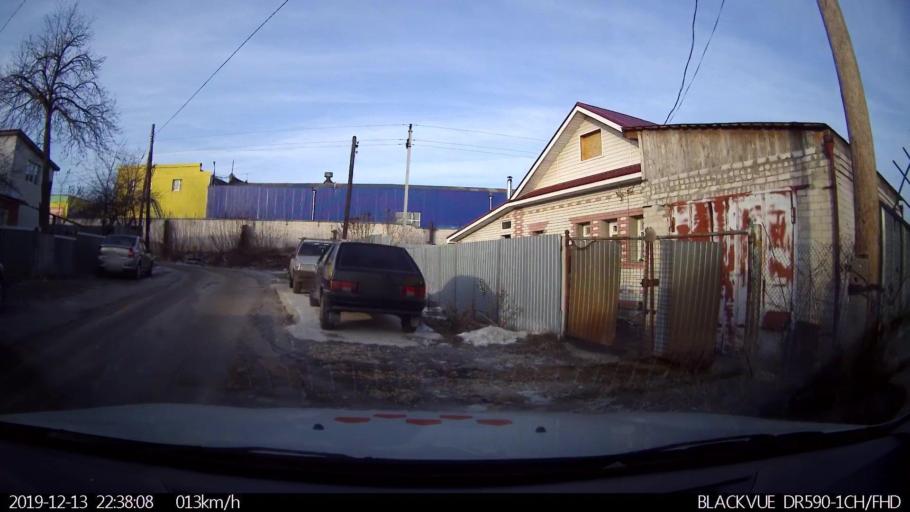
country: RU
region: Nizjnij Novgorod
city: Kstovo
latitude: 56.1754
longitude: 44.1661
